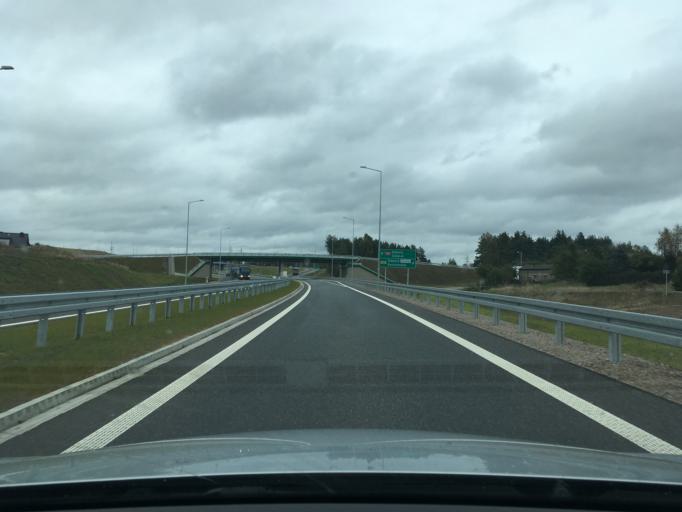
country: PL
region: Pomeranian Voivodeship
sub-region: Powiat koscierski
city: Koscierzyna
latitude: 54.1190
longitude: 18.0163
